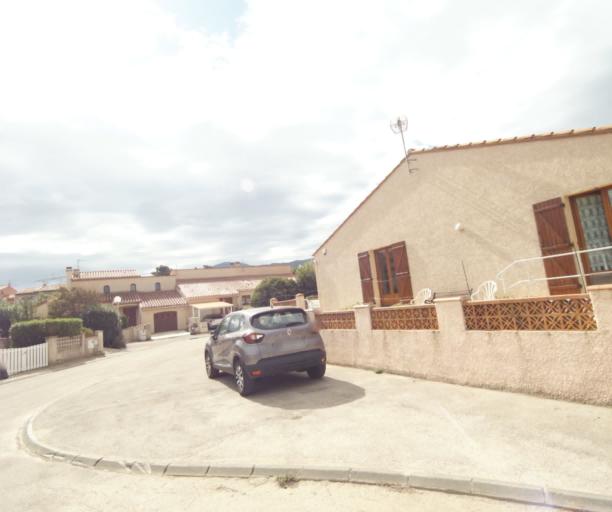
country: FR
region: Languedoc-Roussillon
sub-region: Departement des Pyrenees-Orientales
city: Argelers
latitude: 42.5494
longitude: 3.0266
